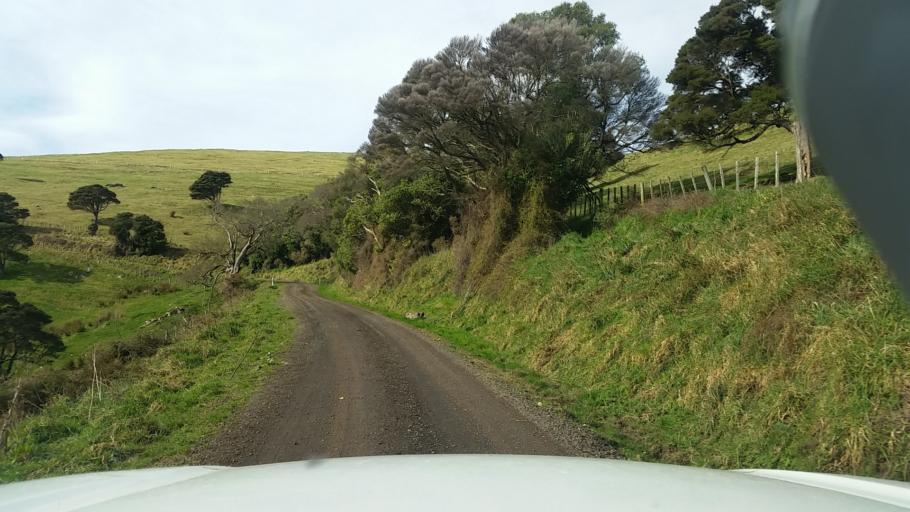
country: NZ
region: Canterbury
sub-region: Christchurch City
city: Christchurch
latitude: -43.6782
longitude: 172.8456
